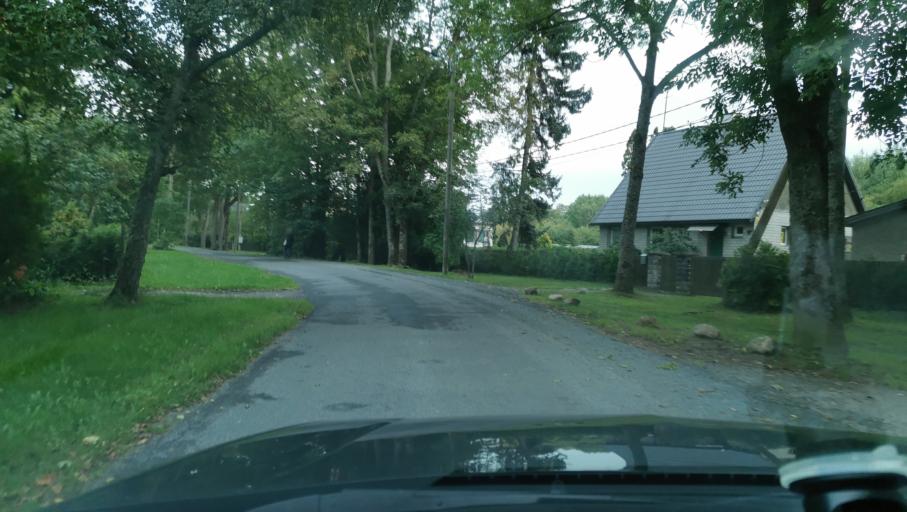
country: EE
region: Harju
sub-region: Saue vald
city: Laagri
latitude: 59.4171
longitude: 24.6276
